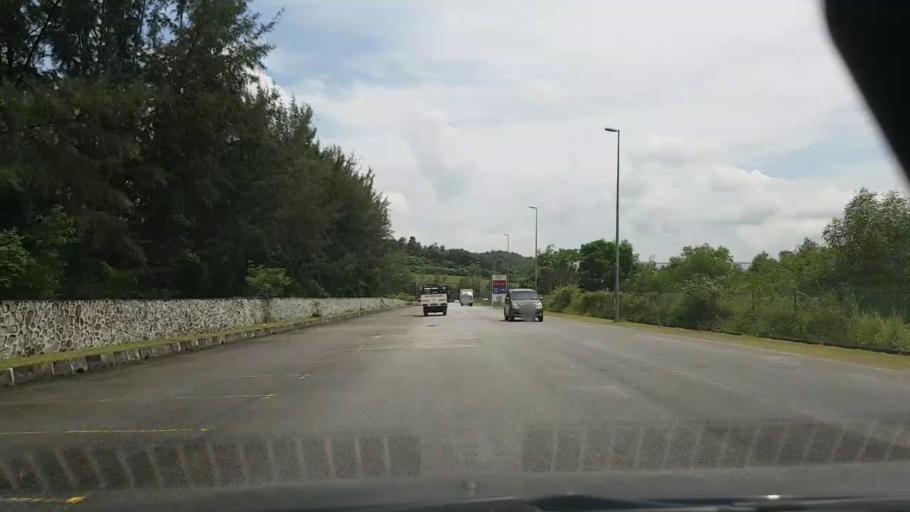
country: MY
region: Selangor
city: Subang Jaya
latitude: 2.9836
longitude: 101.6187
